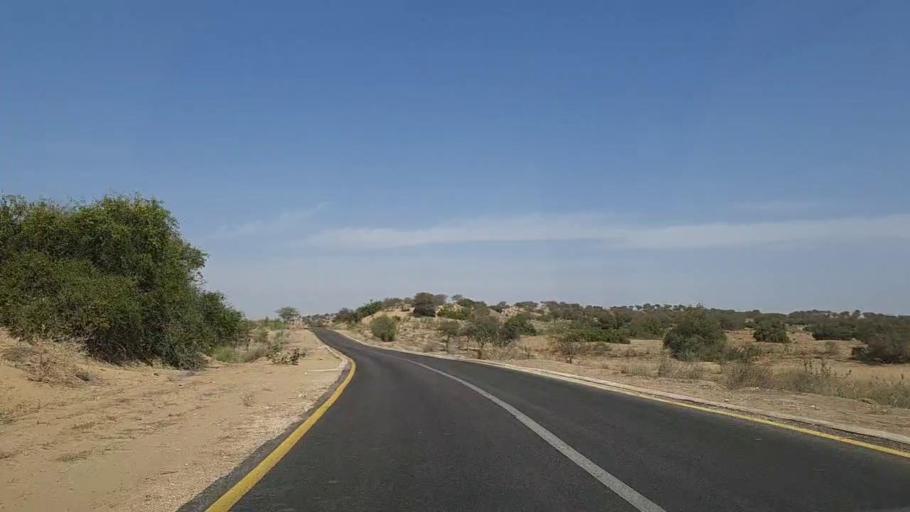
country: PK
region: Sindh
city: Mithi
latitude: 24.9036
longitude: 69.8875
